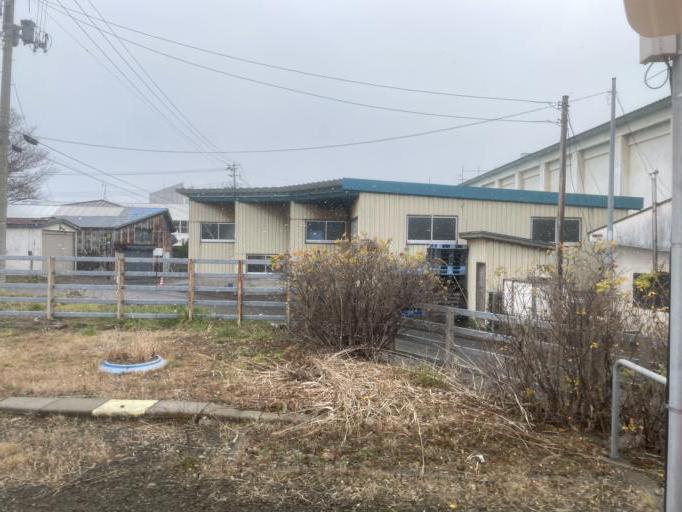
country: JP
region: Aomori
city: Aomori Shi
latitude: 40.9693
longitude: 140.6547
